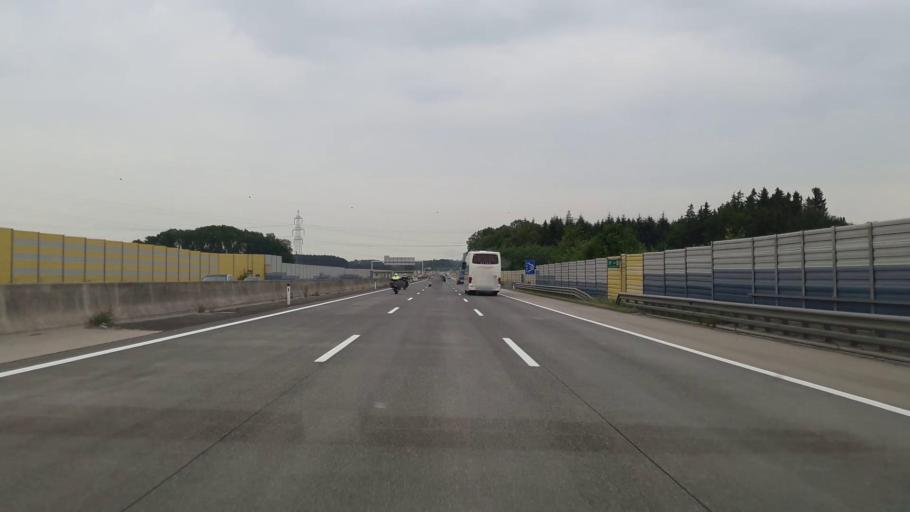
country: AT
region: Upper Austria
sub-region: Wels-Land
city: Sattledt
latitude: 48.0807
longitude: 14.0580
